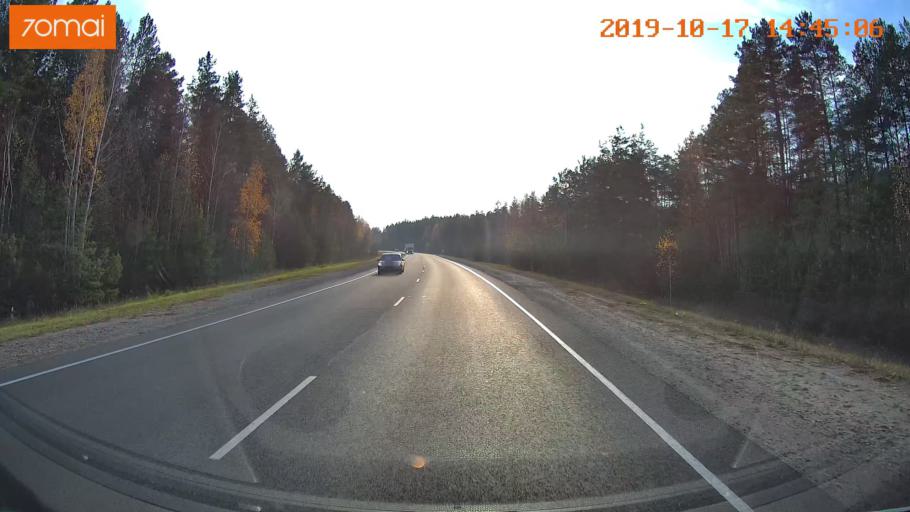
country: RU
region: Rjazan
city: Solotcha
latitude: 54.8046
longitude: 39.8806
